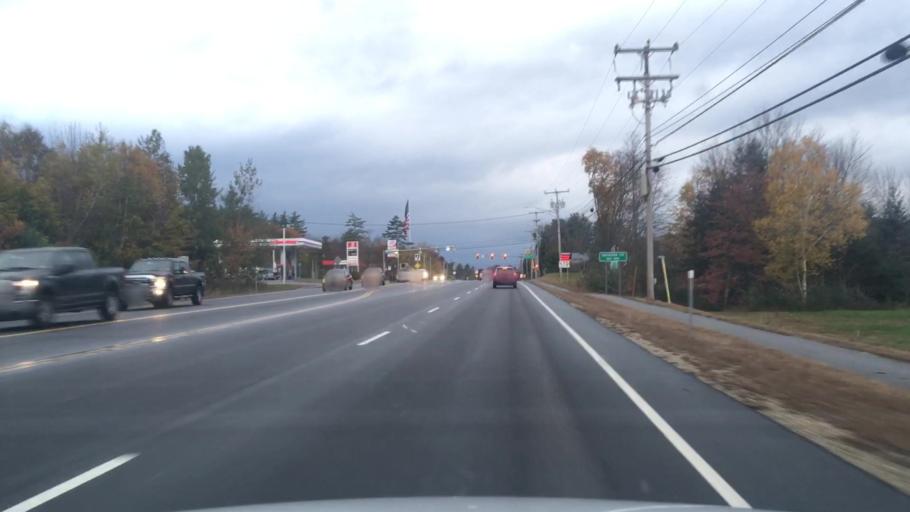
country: US
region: New Hampshire
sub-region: Merrimack County
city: Chichester
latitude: 43.2431
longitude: -71.4024
